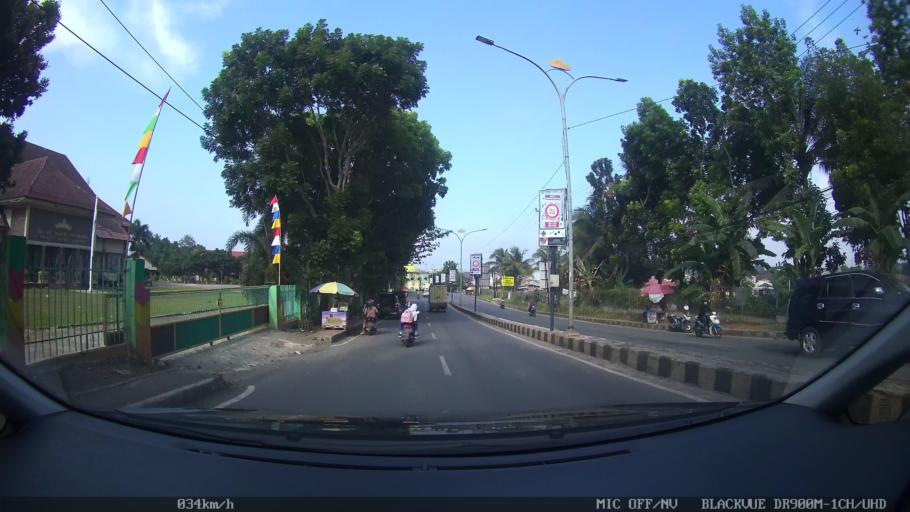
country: ID
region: Lampung
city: Kedaton
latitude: -5.3739
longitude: 105.2243
